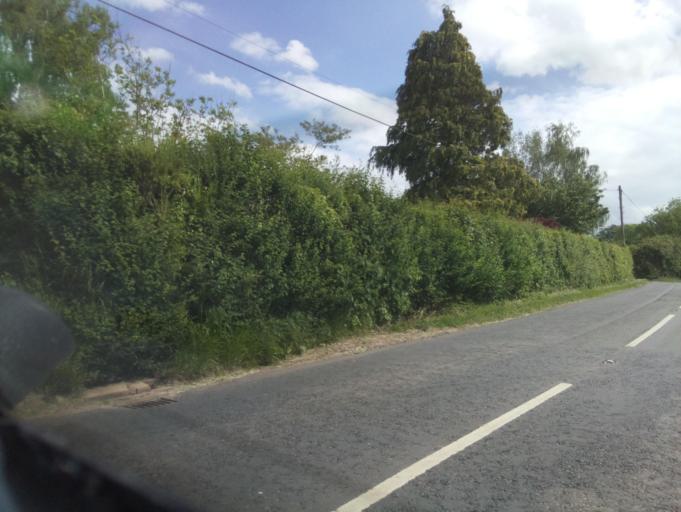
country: GB
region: England
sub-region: Herefordshire
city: Evesbatch
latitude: 52.1149
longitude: -2.4065
